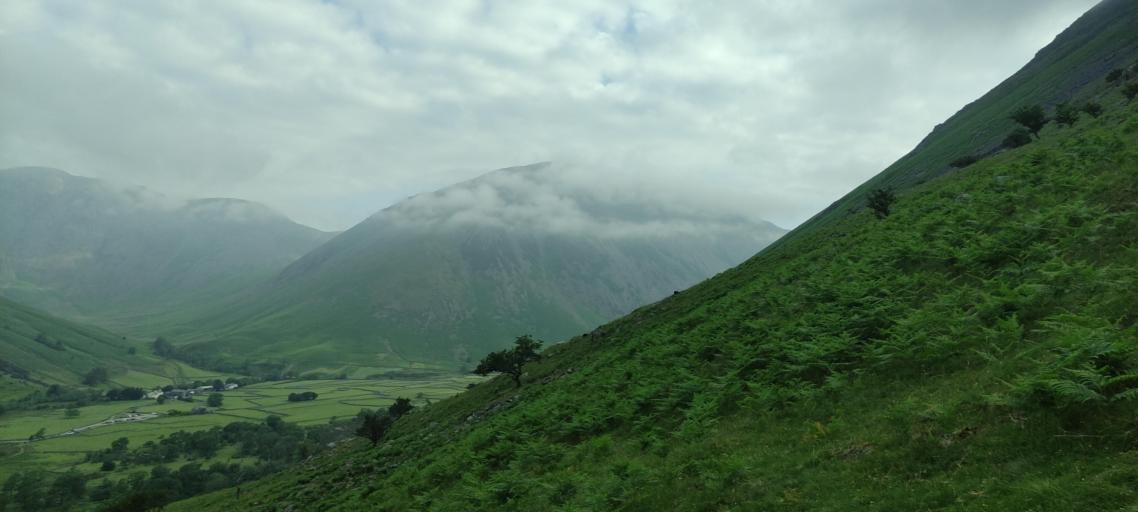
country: GB
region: England
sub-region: Cumbria
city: Keswick
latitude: 54.4556
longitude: -3.2511
